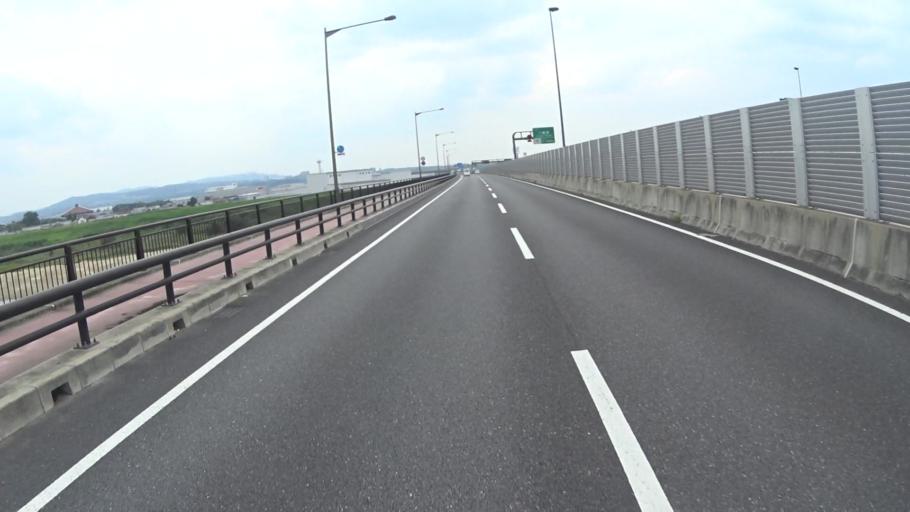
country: JP
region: Kyoto
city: Yawata
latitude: 34.8718
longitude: 135.7440
